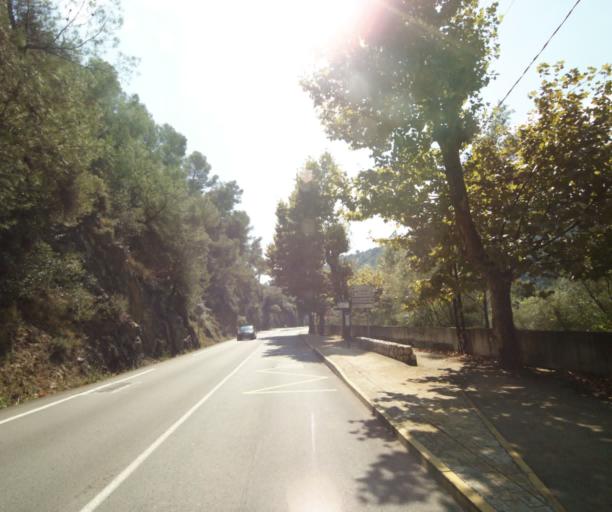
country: FR
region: Provence-Alpes-Cote d'Azur
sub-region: Departement des Alpes-Maritimes
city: Cantaron
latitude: 43.7627
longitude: 7.3217
